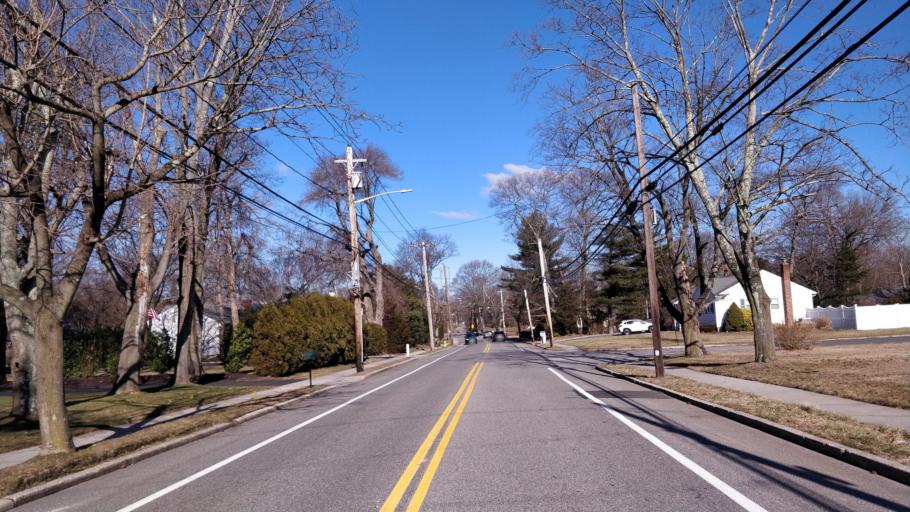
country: US
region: New York
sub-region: Suffolk County
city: Smithtown
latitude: 40.8418
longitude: -73.1957
